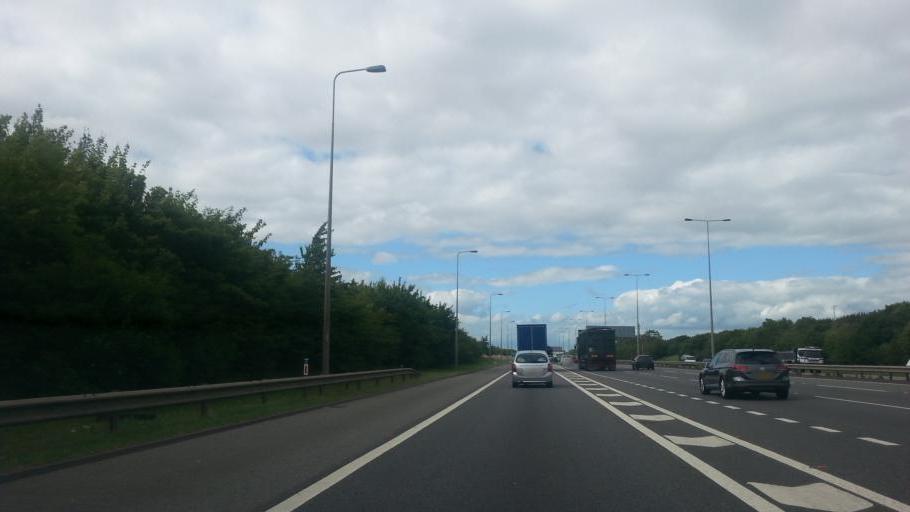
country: GB
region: England
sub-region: Cambridgeshire
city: Great Stukeley
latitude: 52.3862
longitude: -0.2584
